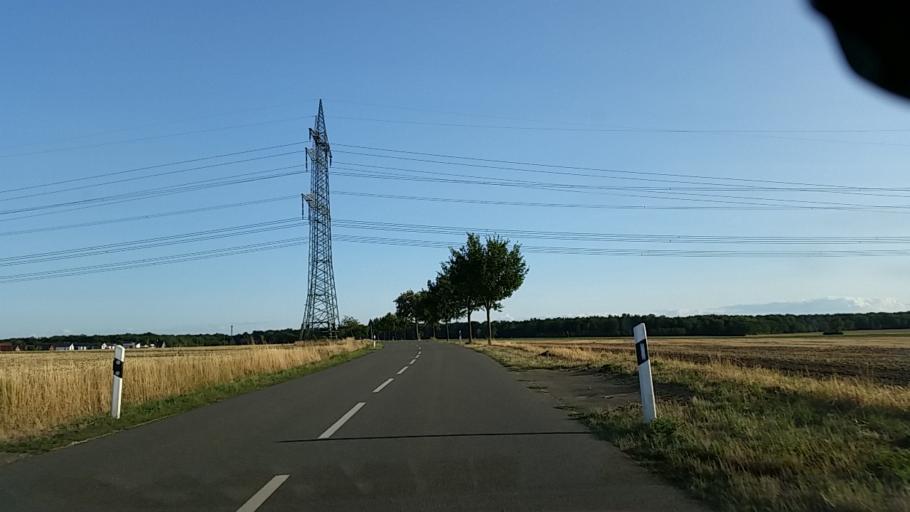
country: DE
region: Lower Saxony
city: Lehre
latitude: 52.3773
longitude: 10.6666
